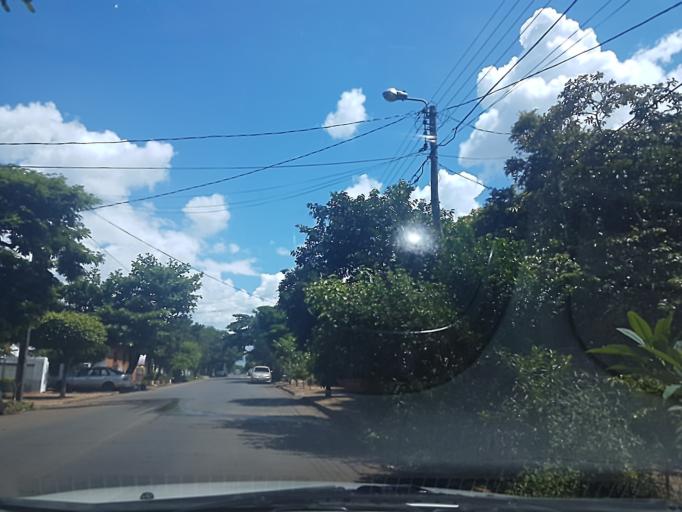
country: PY
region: Central
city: San Lorenzo
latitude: -25.2676
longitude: -57.4834
